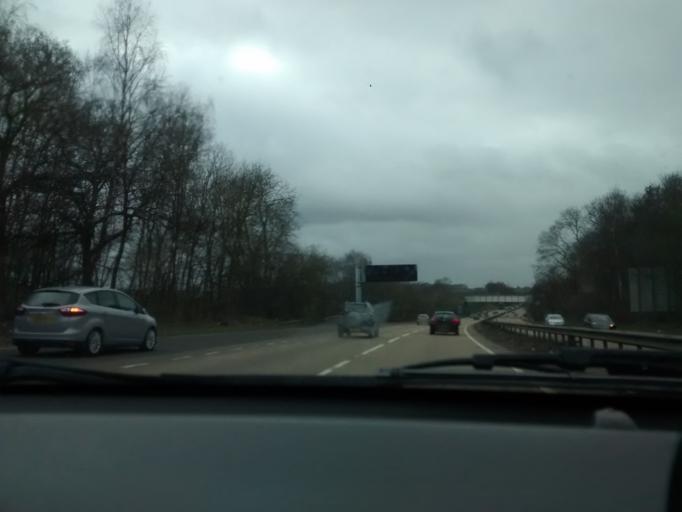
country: GB
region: England
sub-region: Suffolk
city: Ipswich
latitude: 52.0248
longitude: 1.1335
